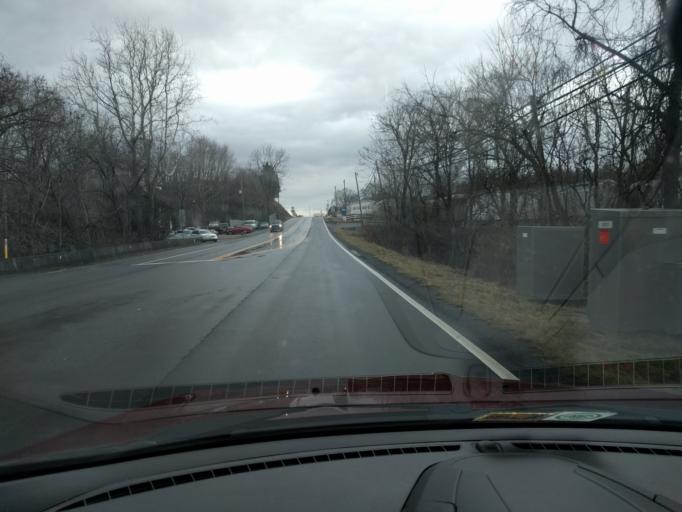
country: US
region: Virginia
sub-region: Botetourt County
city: Cloverdale
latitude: 37.3695
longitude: -79.9087
